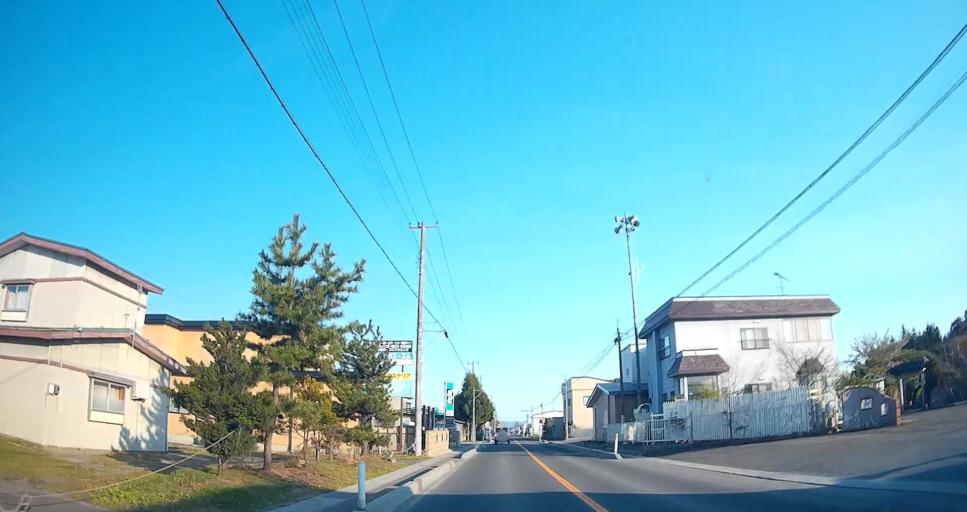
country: JP
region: Aomori
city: Mutsu
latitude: 41.2706
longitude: 141.2183
